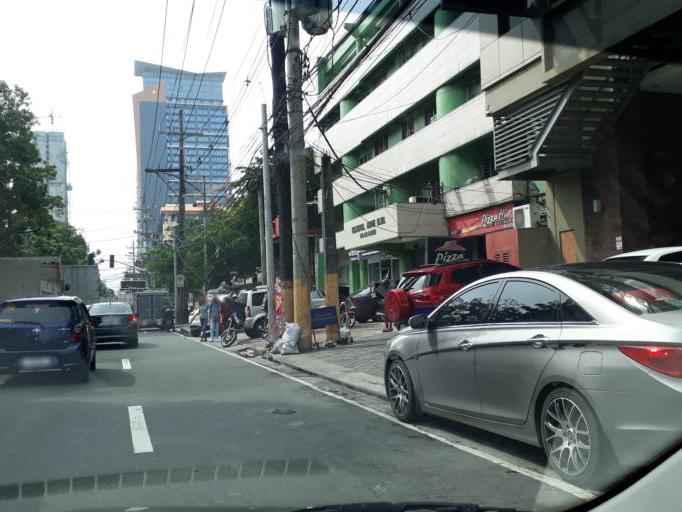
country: PH
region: Metro Manila
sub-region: City of Manila
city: Manila
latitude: 14.6102
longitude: 120.9922
